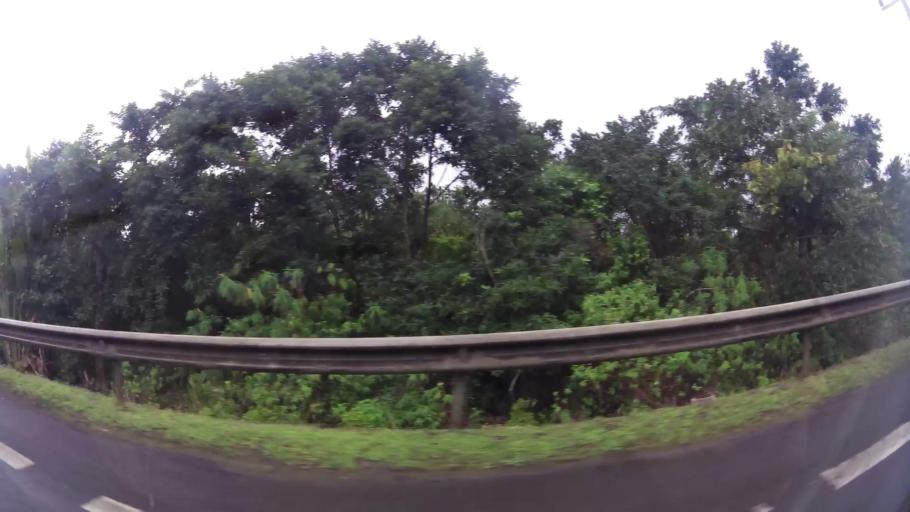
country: MU
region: Plaines Wilhems
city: Curepipe
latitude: -20.3125
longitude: 57.5424
